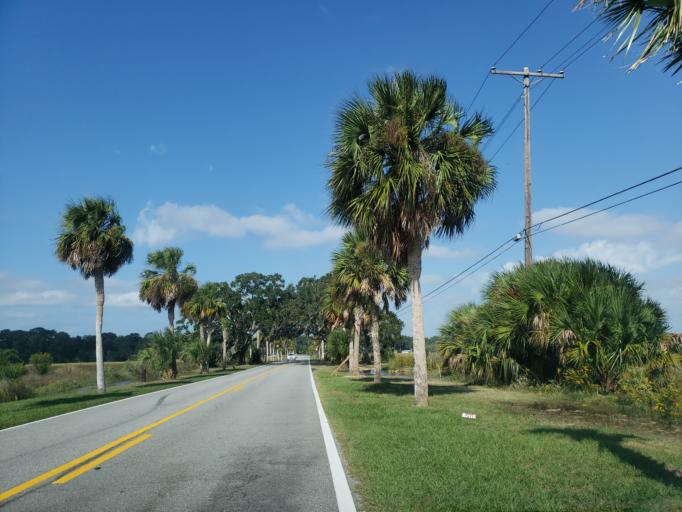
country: US
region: Georgia
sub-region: Chatham County
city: Montgomery
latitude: 31.9341
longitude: -81.0997
